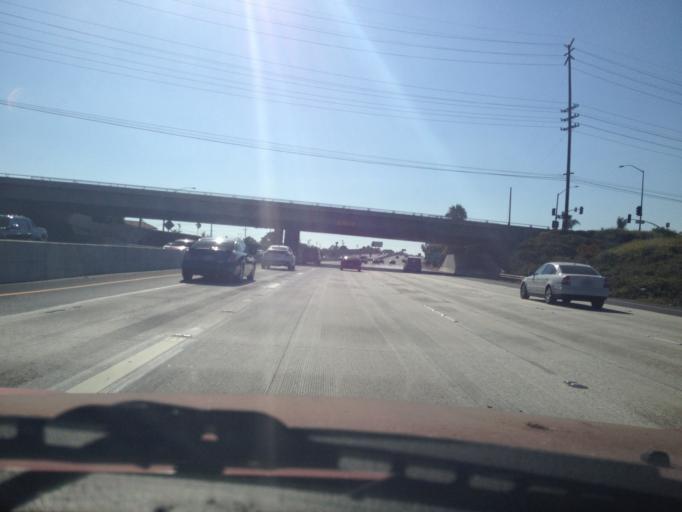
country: US
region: California
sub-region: Orange County
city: La Palma
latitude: 33.8565
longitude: -118.0275
